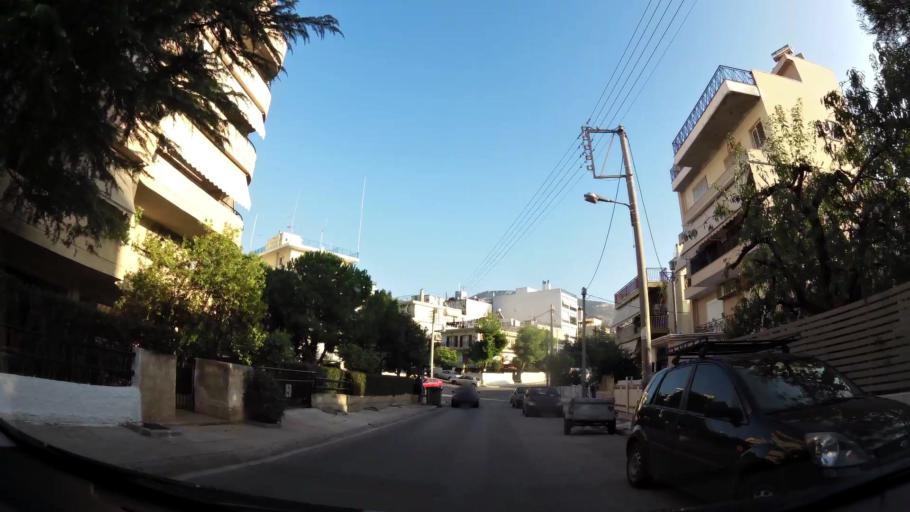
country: GR
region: Attica
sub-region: Nomarchia Athinas
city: Argyroupoli
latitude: 37.8984
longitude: 23.7737
